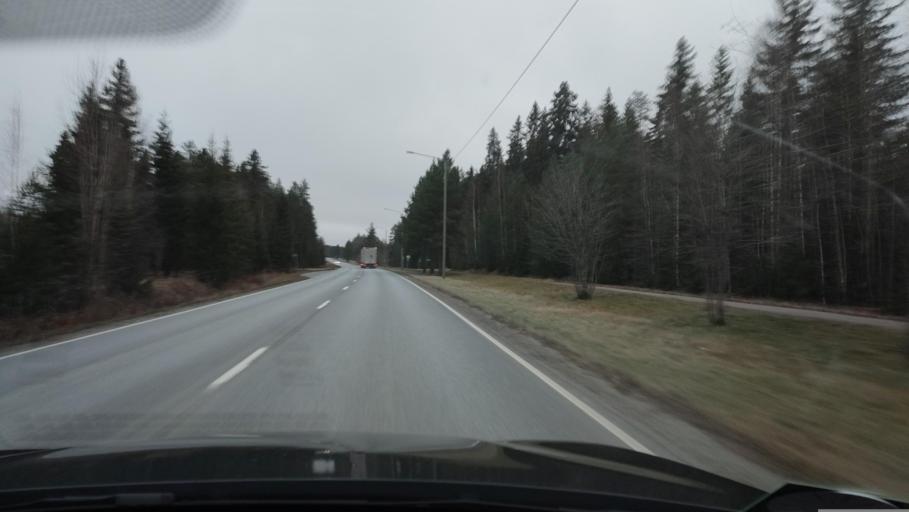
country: FI
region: Southern Ostrobothnia
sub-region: Suupohja
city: Kauhajoki
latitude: 62.4027
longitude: 22.1602
